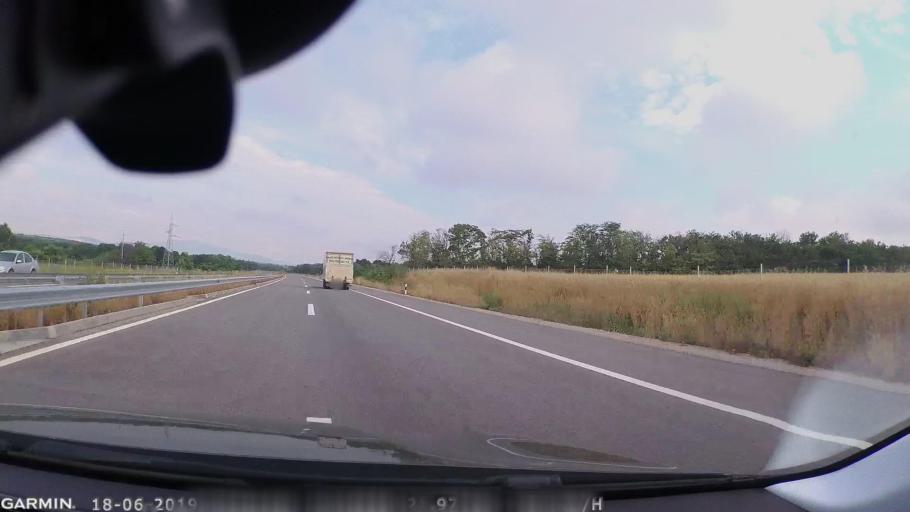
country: MK
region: Sveti Nikole
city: Sveti Nikole
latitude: 41.8445
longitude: 21.9762
